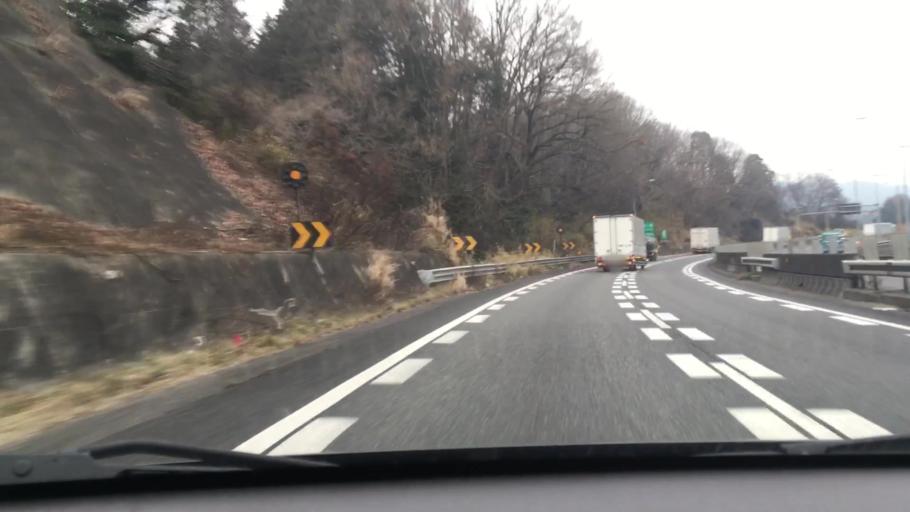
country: JP
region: Mie
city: Nabari
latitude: 34.6891
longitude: 136.0479
